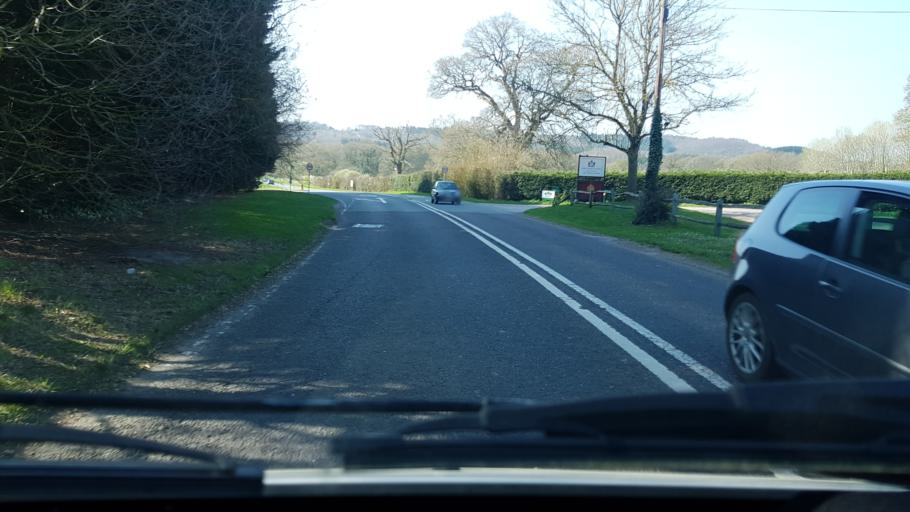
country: GB
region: England
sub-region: West Sussex
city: Fernhurst
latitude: 51.0348
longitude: -0.7251
